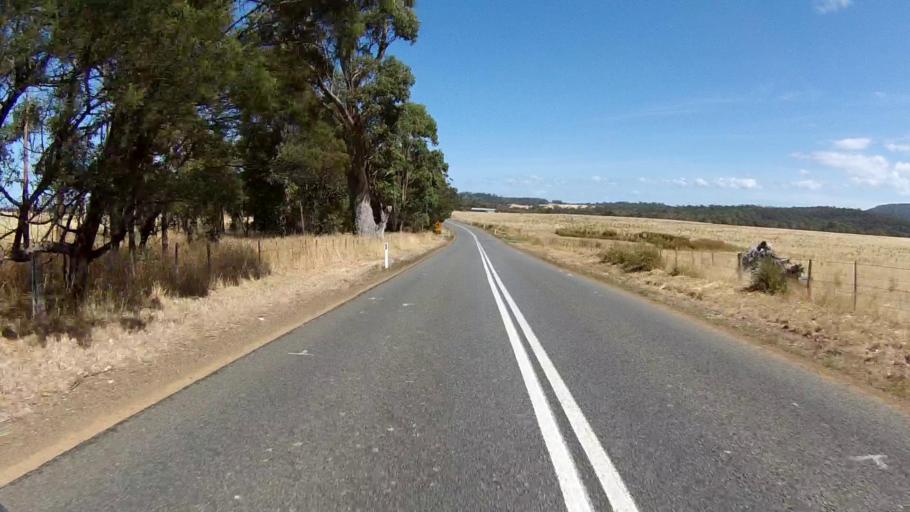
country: AU
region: Tasmania
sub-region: Sorell
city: Sorell
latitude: -42.2519
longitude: 148.0068
